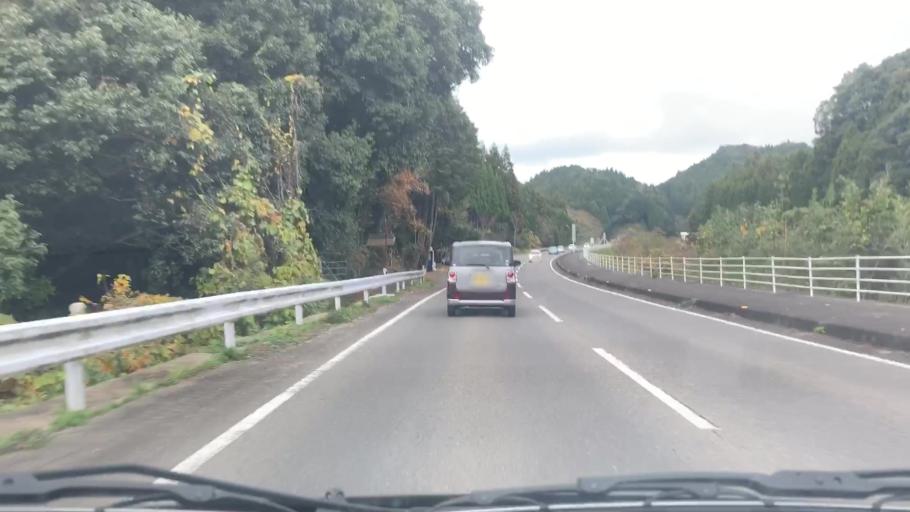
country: JP
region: Saga Prefecture
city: Ureshinomachi-shimojuku
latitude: 33.0940
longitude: 130.0290
